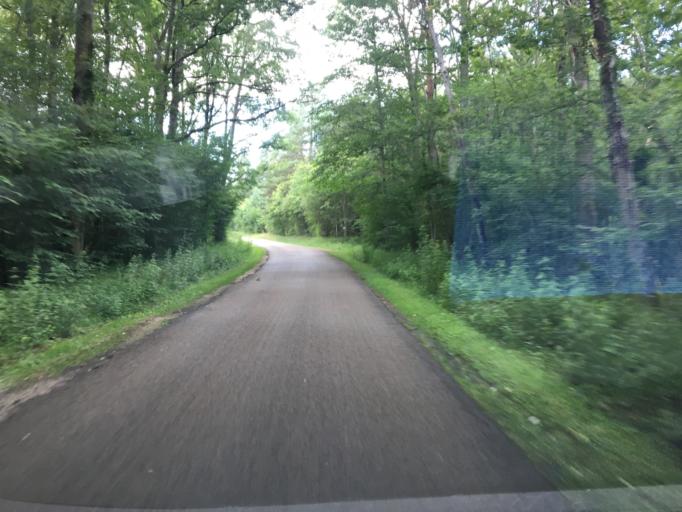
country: FR
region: Bourgogne
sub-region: Departement de l'Yonne
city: Fleury-la-Vallee
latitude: 47.8586
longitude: 3.4864
